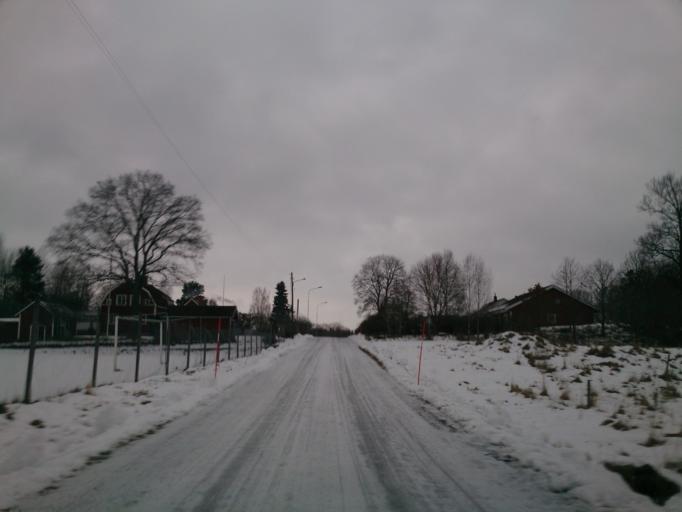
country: SE
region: OEstergoetland
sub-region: Atvidabergs Kommun
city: Atvidaberg
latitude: 58.3313
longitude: 16.0232
